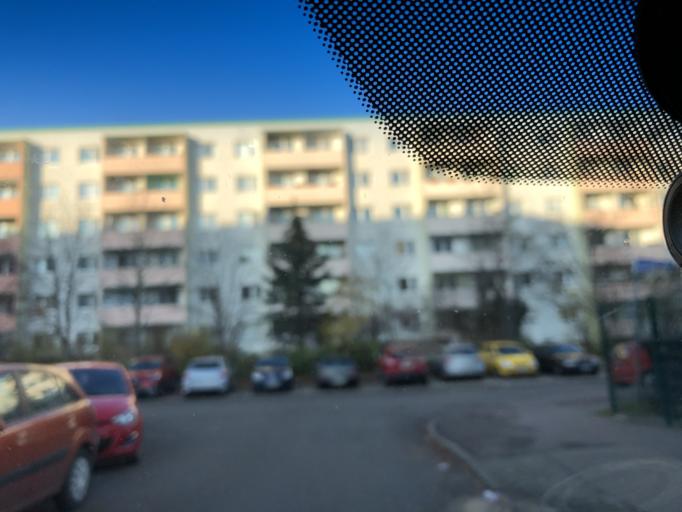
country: DE
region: Saxony-Anhalt
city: Halle Neustadt
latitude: 51.4808
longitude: 11.9075
